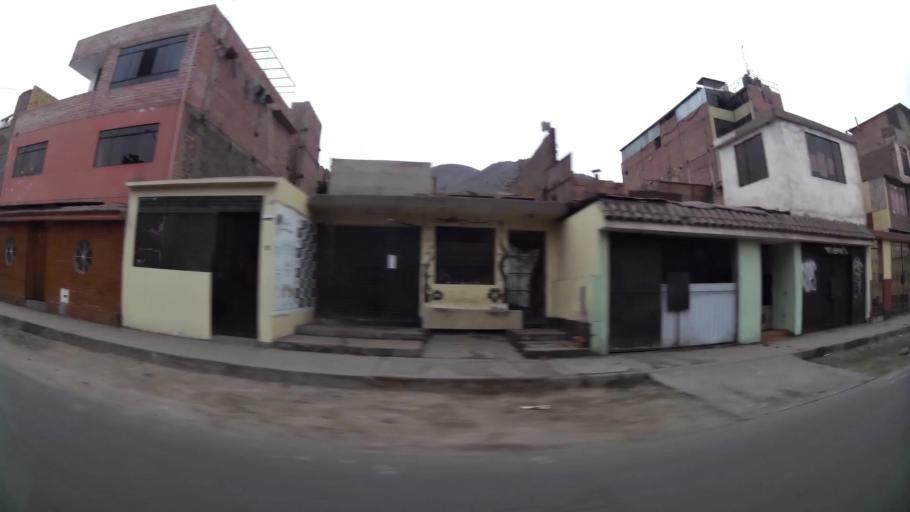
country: PE
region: Lima
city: Lima
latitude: -12.0177
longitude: -76.9835
